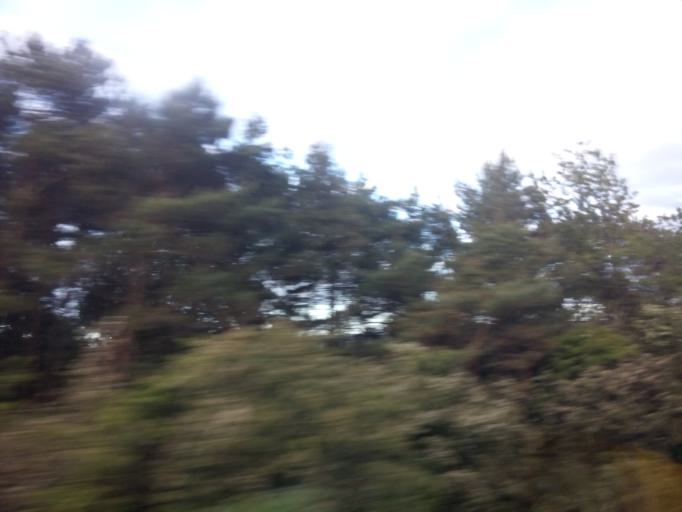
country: GB
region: England
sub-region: County Durham
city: Durham
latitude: 54.8157
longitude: -1.5752
